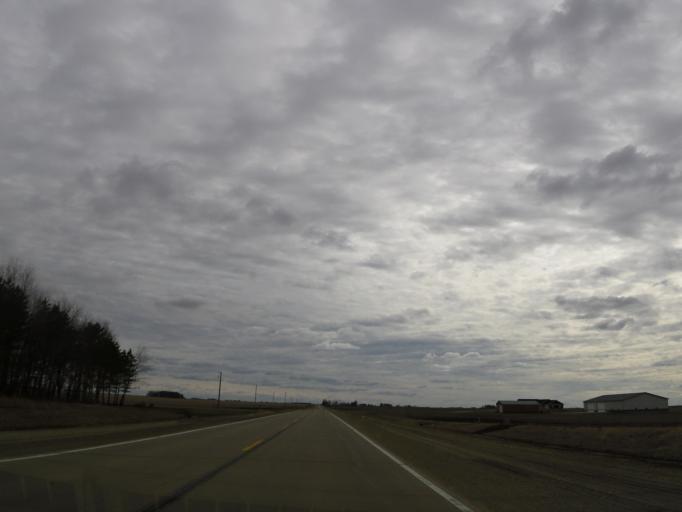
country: US
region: Iowa
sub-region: Howard County
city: Cresco
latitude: 43.4222
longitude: -92.2986
